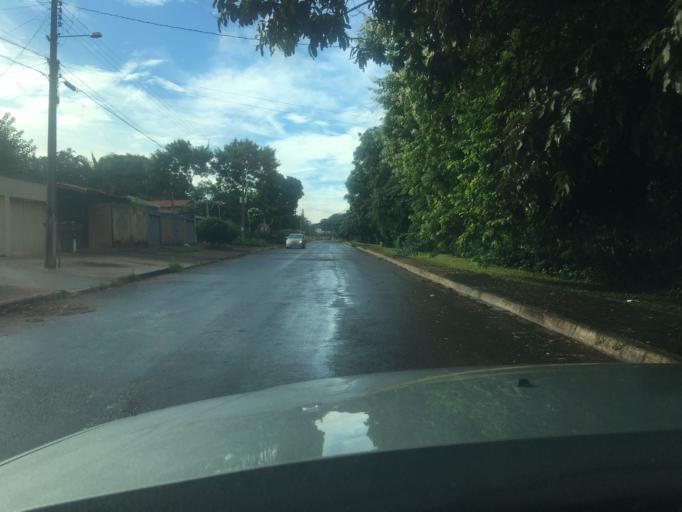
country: BR
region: Goias
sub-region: Aparecida De Goiania
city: Aparecida de Goiania
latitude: -16.7996
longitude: -49.2469
